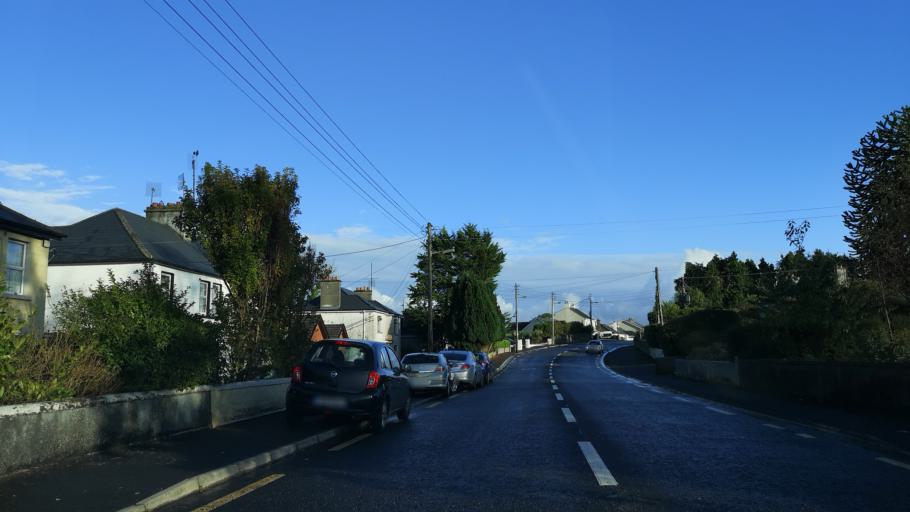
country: IE
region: Connaught
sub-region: Roscommon
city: Castlerea
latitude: 53.7653
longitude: -8.4804
